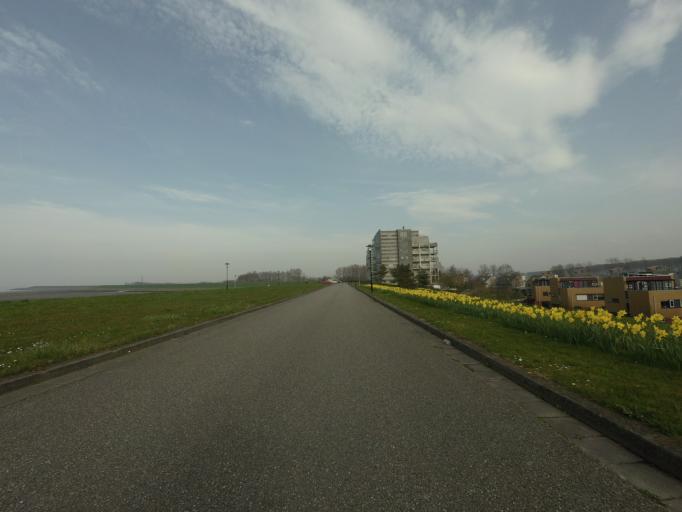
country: NL
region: Zeeland
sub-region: Gemeente Terneuzen
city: Terneuzen
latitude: 51.3356
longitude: 3.8635
